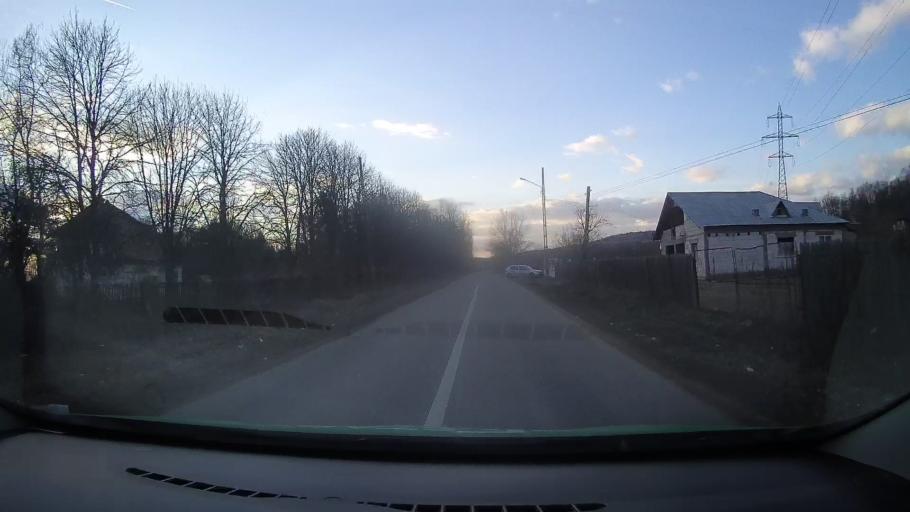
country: RO
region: Dambovita
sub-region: Comuna Gura Ocnitei
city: Gura Ocnitei
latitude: 44.9367
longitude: 25.5852
